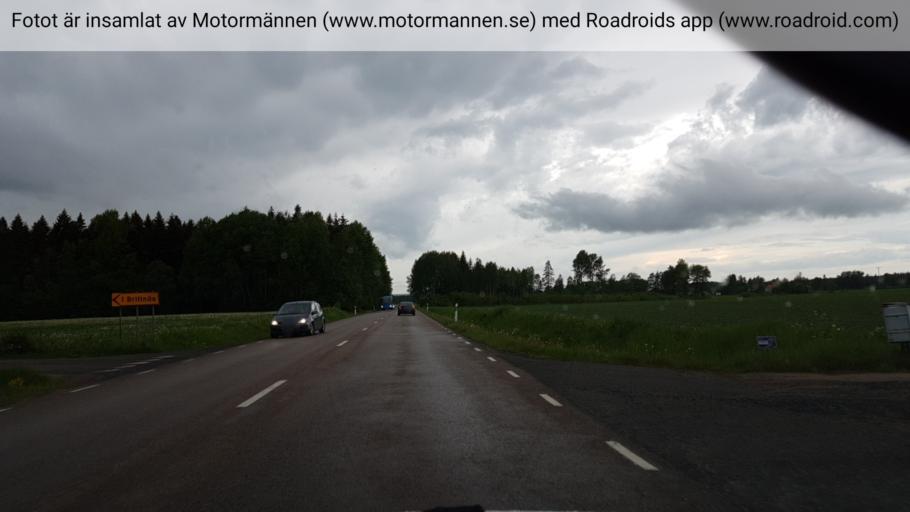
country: SE
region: Vaestra Goetaland
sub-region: Tidaholms Kommun
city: Olofstorp
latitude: 58.3669
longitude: 14.0153
